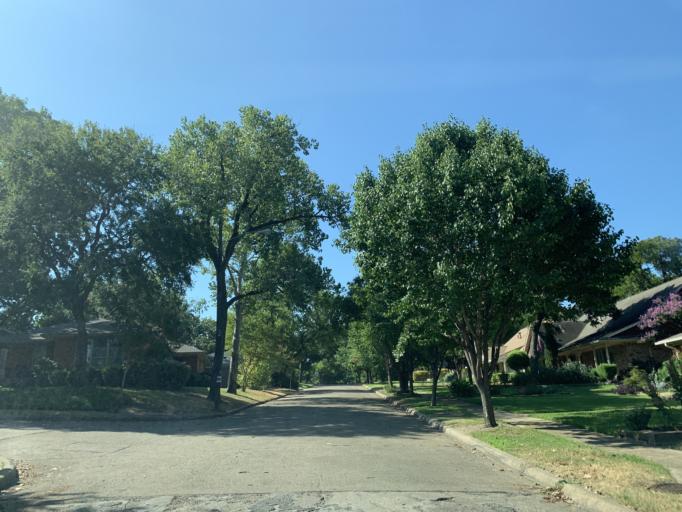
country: US
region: Texas
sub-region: Dallas County
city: Cockrell Hill
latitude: 32.7461
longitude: -96.8645
